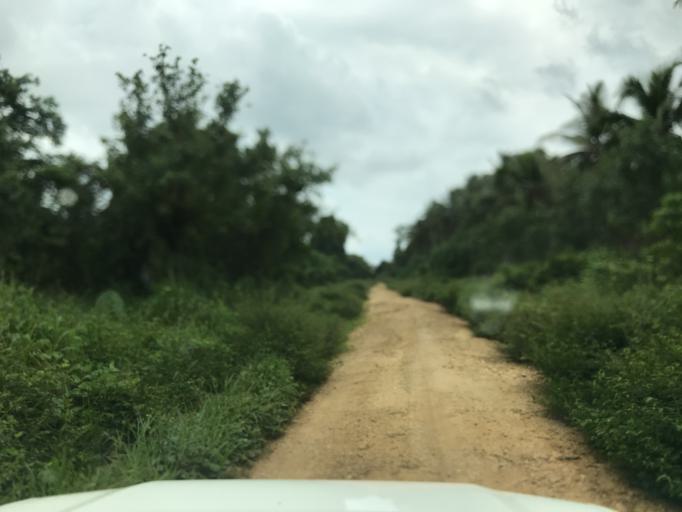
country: VU
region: Sanma
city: Port-Olry
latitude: -15.1857
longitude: 167.0256
